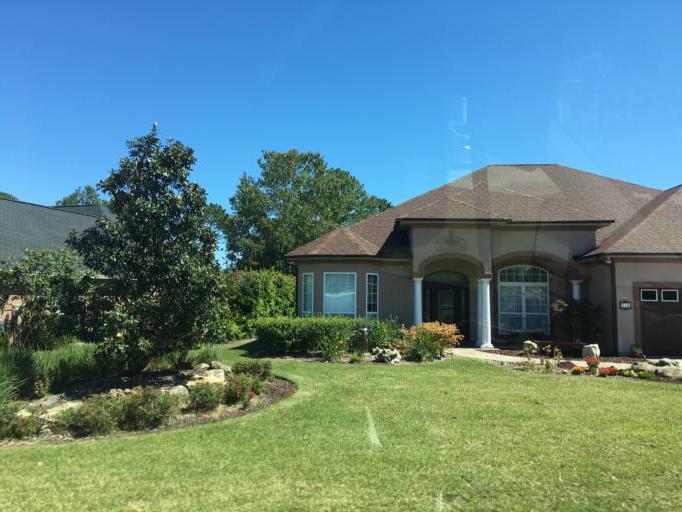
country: US
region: Florida
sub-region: Bay County
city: Panama City Beach
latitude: 30.1904
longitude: -85.8103
